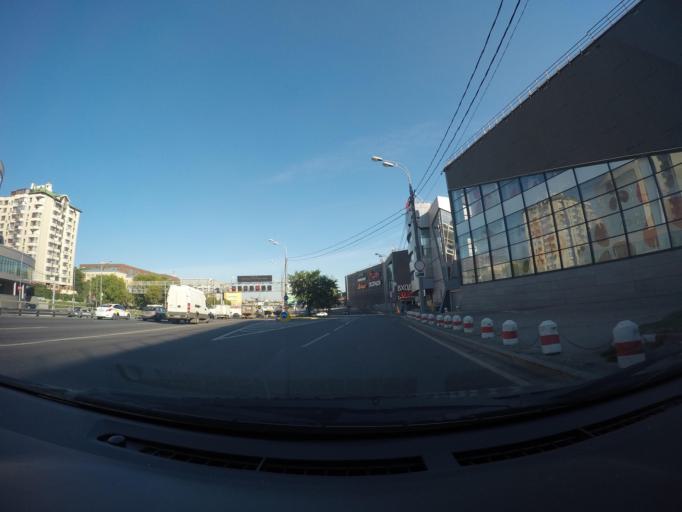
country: RU
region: Moscow
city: Sokol'niki
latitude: 55.7848
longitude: 37.6646
